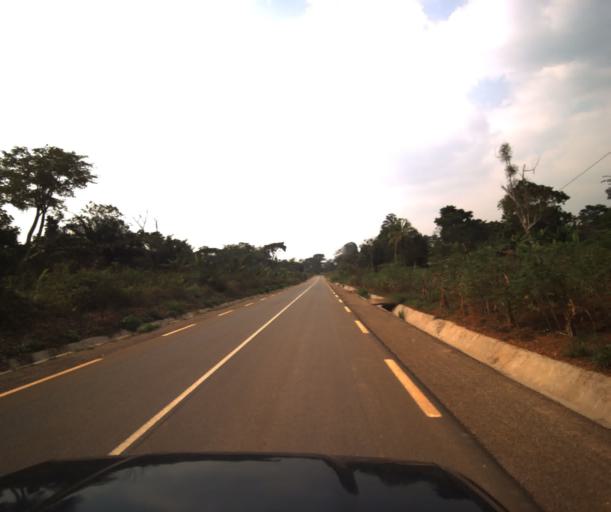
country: CM
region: Centre
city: Mbankomo
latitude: 3.7375
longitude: 11.3946
